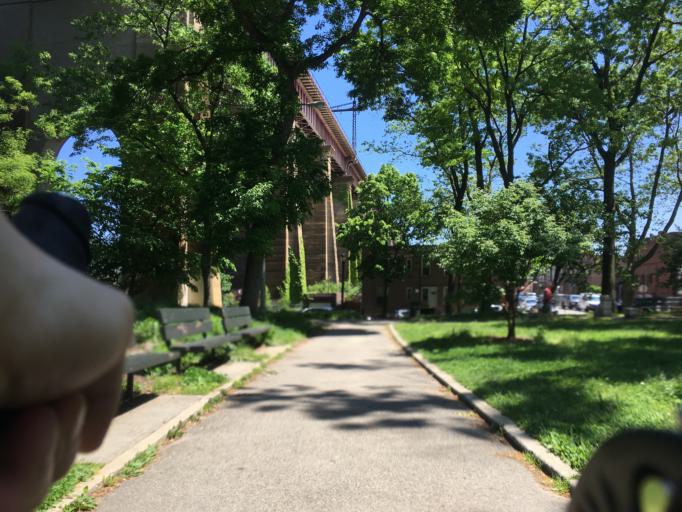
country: US
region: New York
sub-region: Queens County
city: Long Island City
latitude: 40.7806
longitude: -73.9198
